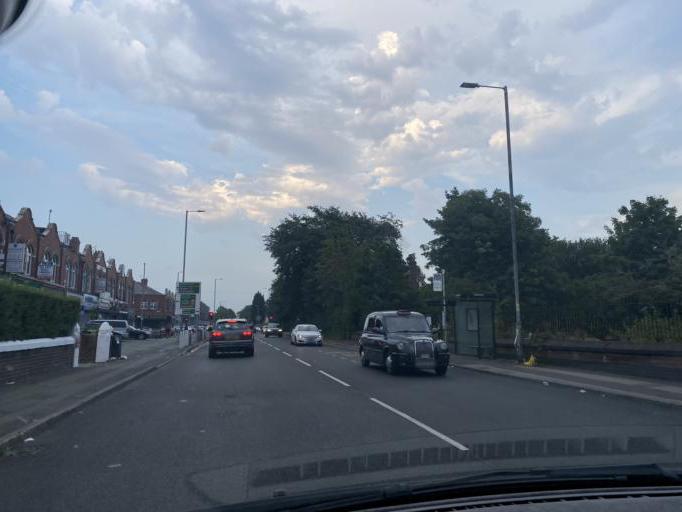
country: GB
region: England
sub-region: Manchester
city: Longsight
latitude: 53.4535
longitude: -2.2132
